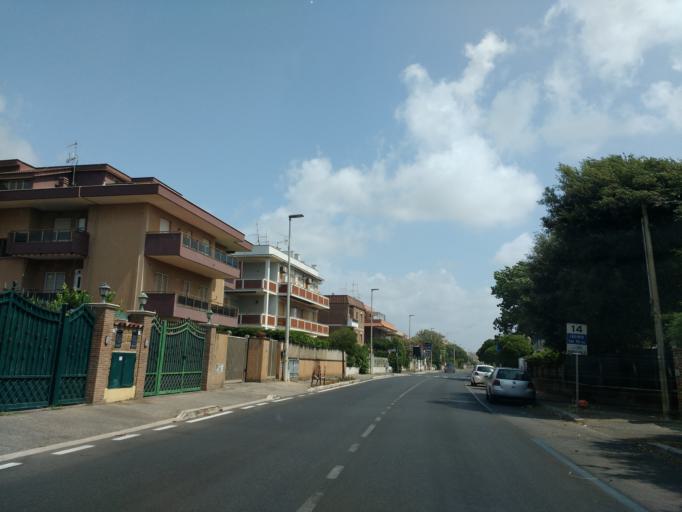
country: IT
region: Latium
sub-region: Citta metropolitana di Roma Capitale
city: Torvaianica
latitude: 41.6320
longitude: 12.4499
